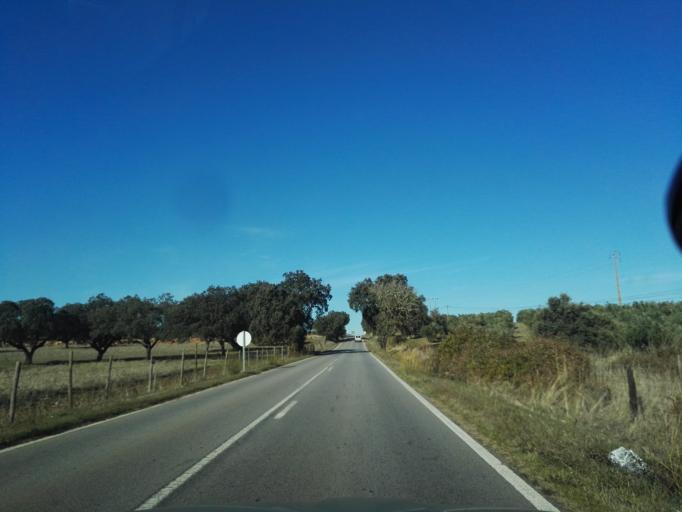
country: PT
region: Portalegre
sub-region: Elvas
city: Elvas
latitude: 38.9134
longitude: -7.1819
